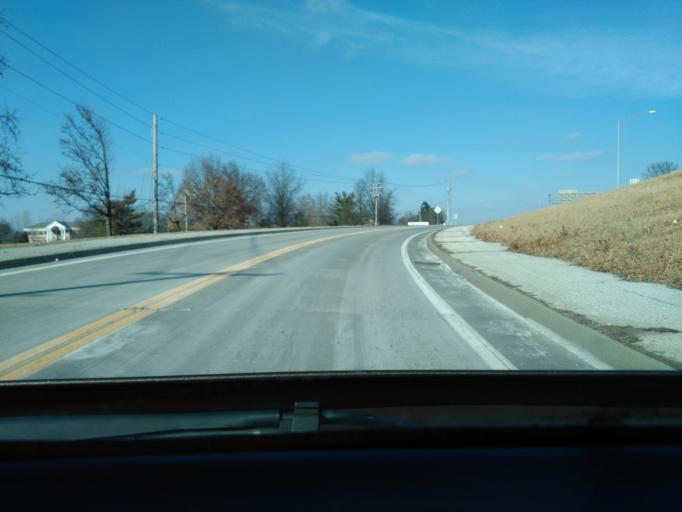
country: US
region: Missouri
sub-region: Saint Louis County
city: Manchester
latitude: 38.6286
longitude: -90.5152
